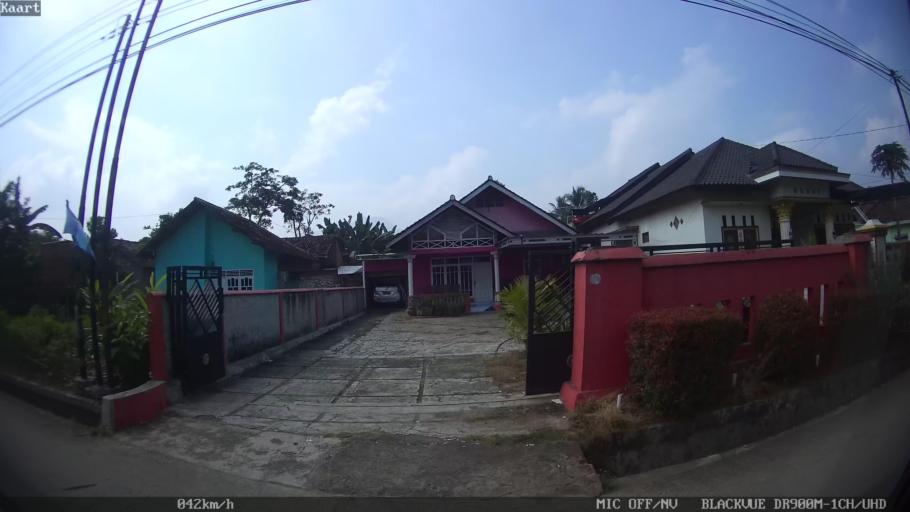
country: ID
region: Lampung
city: Gedongtataan
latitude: -5.3786
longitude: 105.1252
